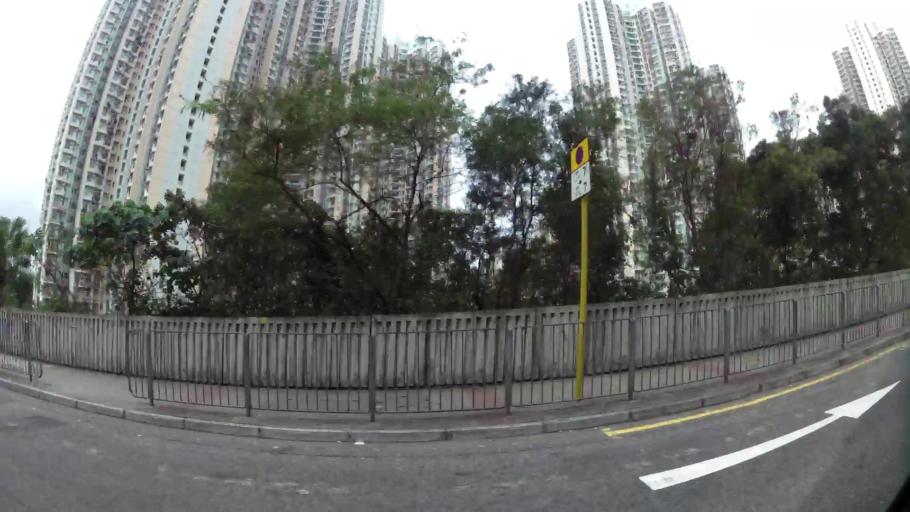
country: HK
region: Kowloon City
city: Kowloon
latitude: 22.3164
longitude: 114.2361
